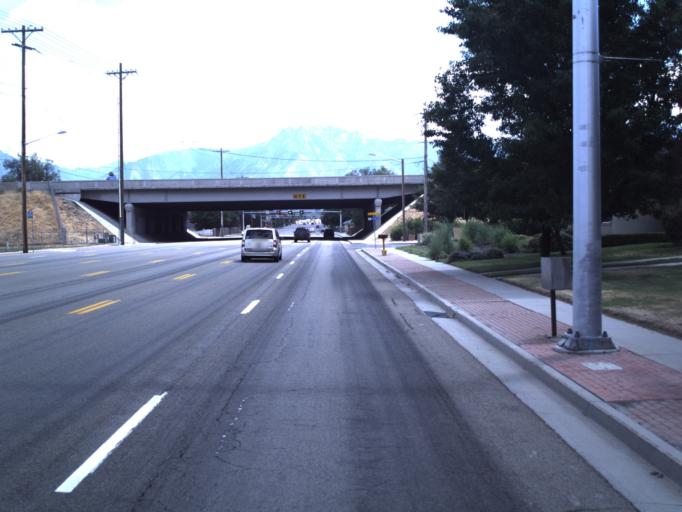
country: US
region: Utah
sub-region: Salt Lake County
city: Taylorsville
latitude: 40.6529
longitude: -111.9544
